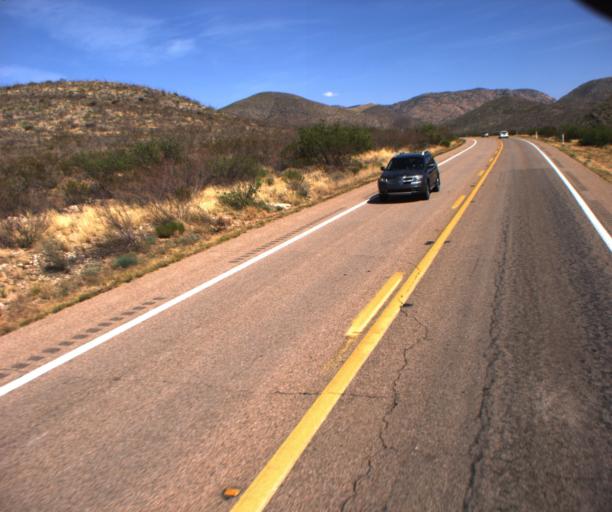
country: US
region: Arizona
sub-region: Cochise County
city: Bisbee
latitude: 31.5236
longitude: -110.0431
